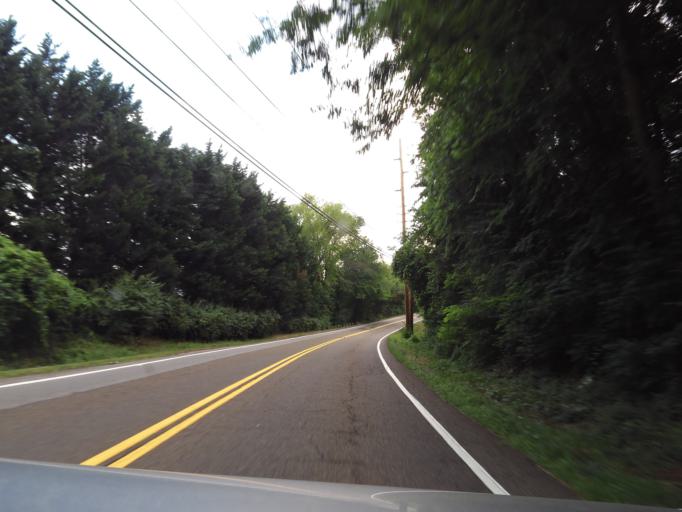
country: US
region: Tennessee
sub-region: Blount County
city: Louisville
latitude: 35.8510
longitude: -84.1012
